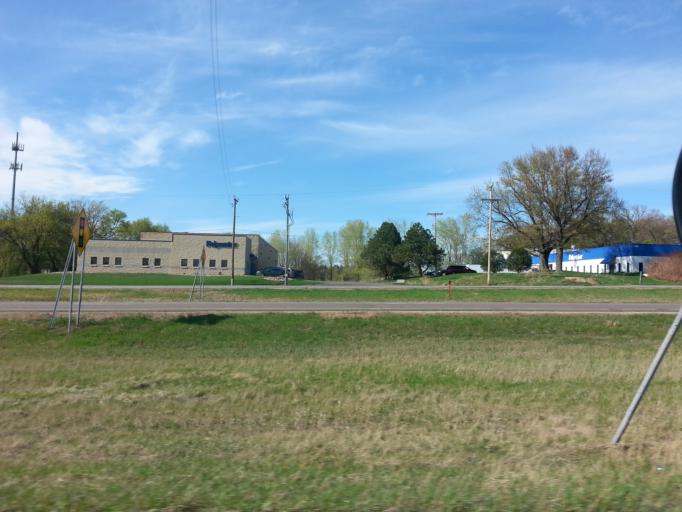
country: US
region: Minnesota
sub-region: Washington County
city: Lake Elmo
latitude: 45.0356
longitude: -92.8797
